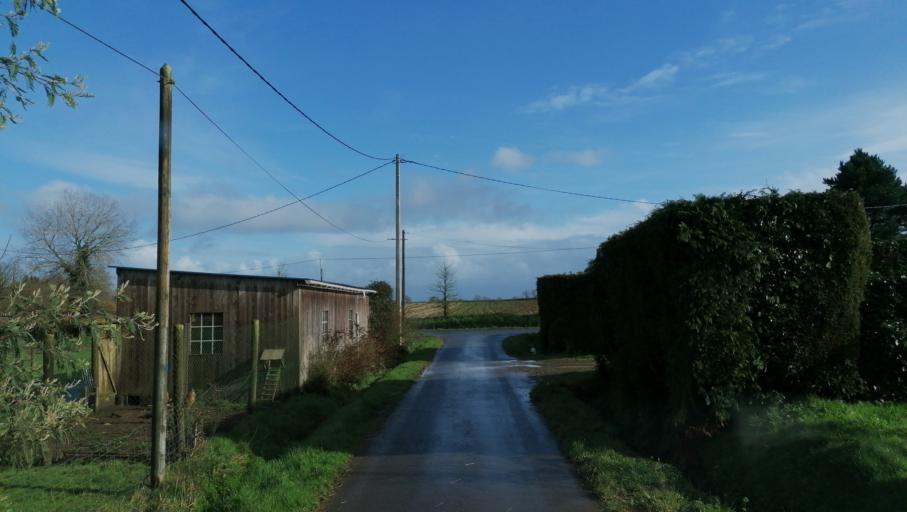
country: FR
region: Brittany
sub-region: Departement des Cotes-d'Armor
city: Lanrodec
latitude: 48.4947
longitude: -3.0127
